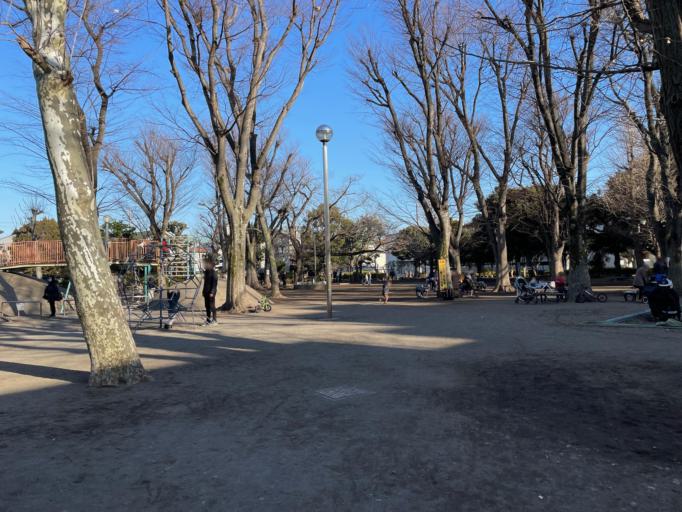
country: JP
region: Tokyo
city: Tokyo
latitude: 35.6323
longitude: 139.6963
